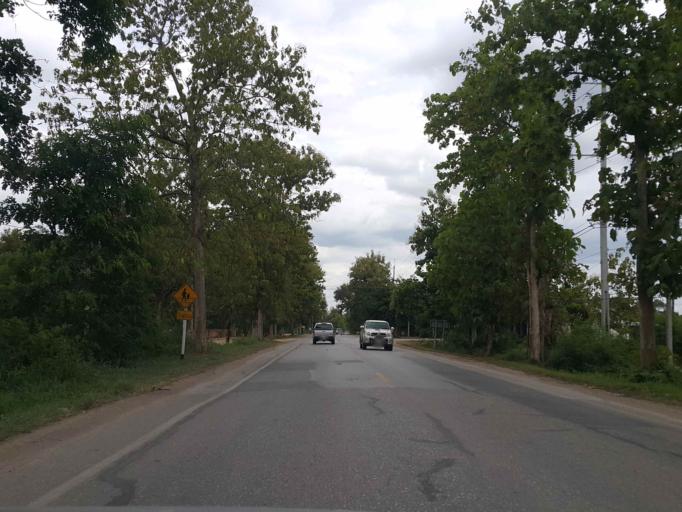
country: TH
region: Chiang Mai
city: Doi Lo
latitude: 18.4333
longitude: 98.8700
